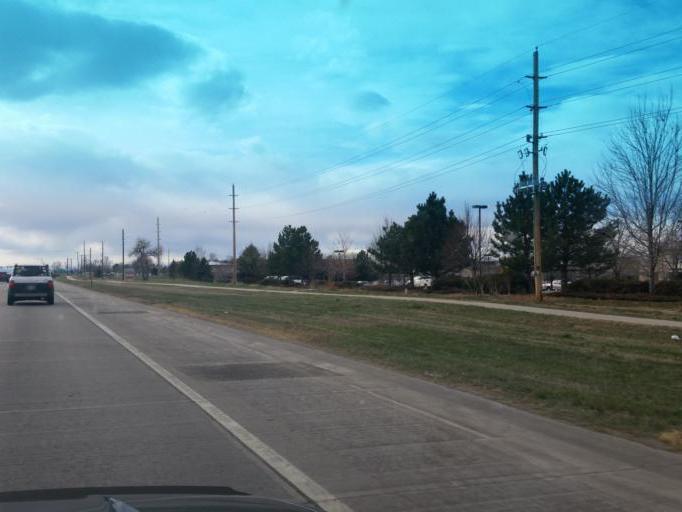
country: US
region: Colorado
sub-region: Weld County
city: Greeley
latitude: 40.3922
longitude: -104.7499
